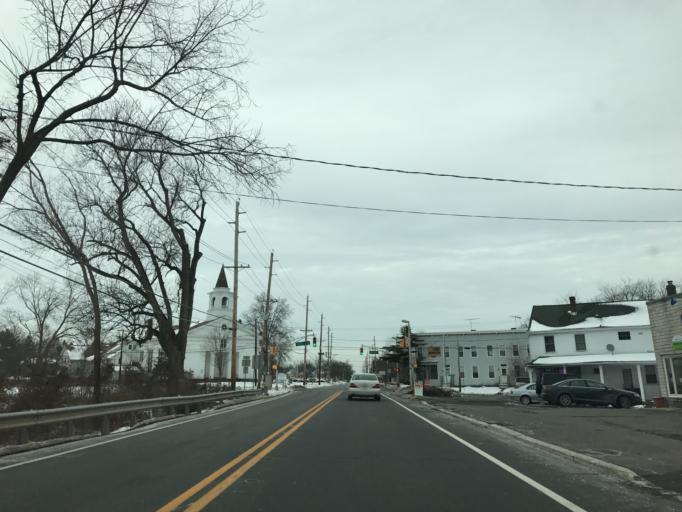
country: US
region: New Jersey
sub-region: Somerset County
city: Bloomingdale
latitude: 40.4471
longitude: -74.6627
